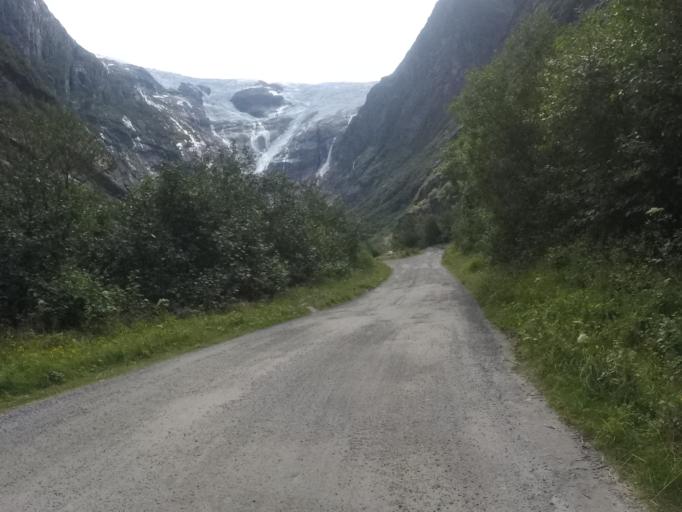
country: NO
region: Sogn og Fjordane
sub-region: Stryn
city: Stryn
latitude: 61.7566
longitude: 7.0376
